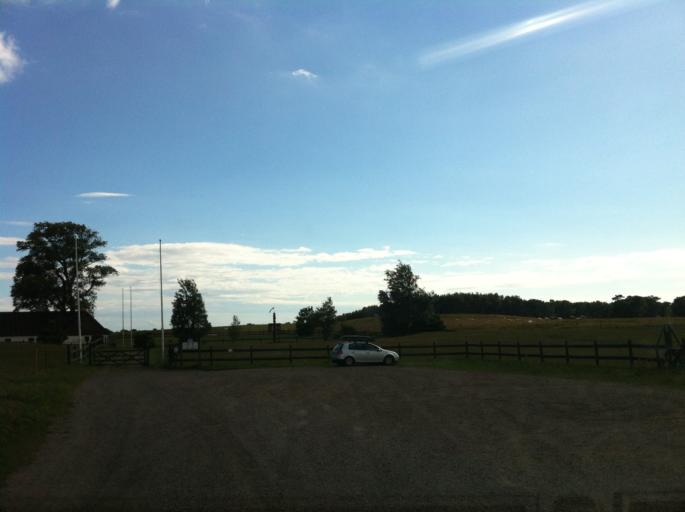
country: SE
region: Skane
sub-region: Ystads Kommun
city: Kopingebro
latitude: 55.3903
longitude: 14.0548
